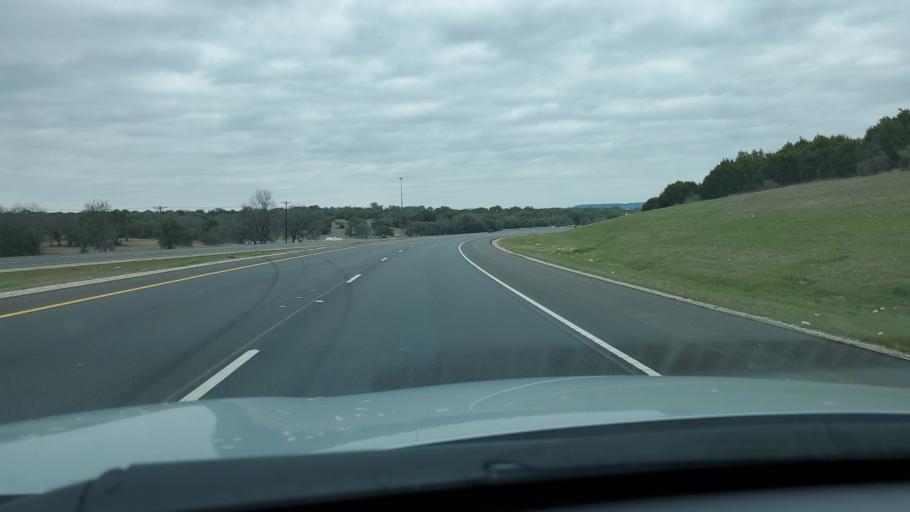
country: US
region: Texas
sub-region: Williamson County
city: Florence
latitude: 30.9534
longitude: -97.7863
